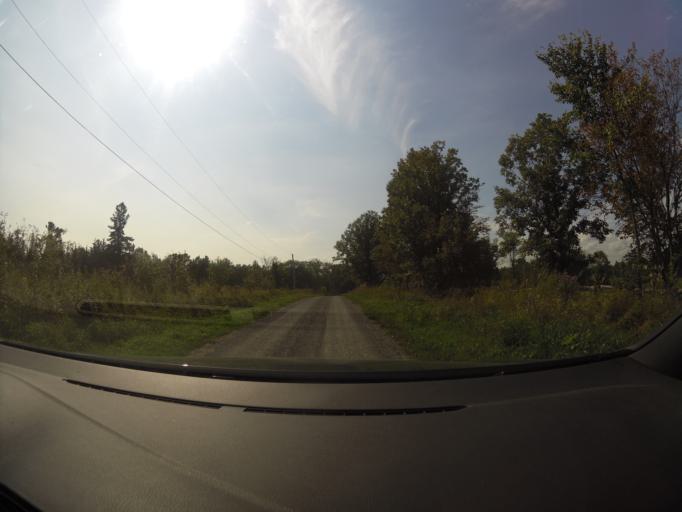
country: CA
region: Ontario
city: Carleton Place
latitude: 45.2772
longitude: -76.2507
